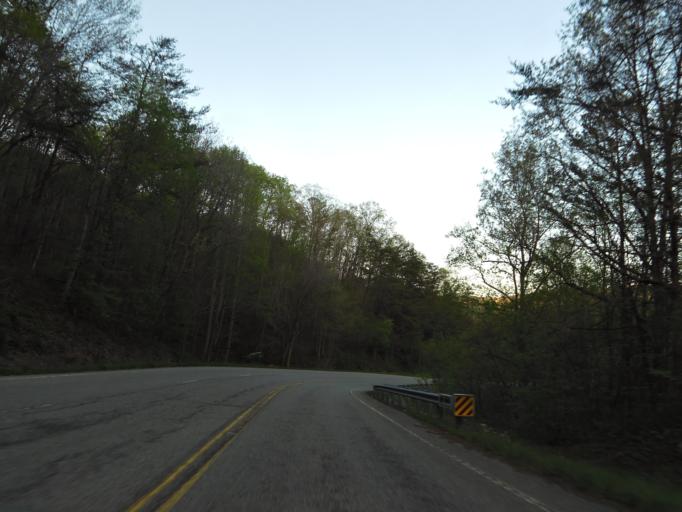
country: US
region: Tennessee
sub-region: Campbell County
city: Fincastle
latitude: 36.4535
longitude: -84.0775
